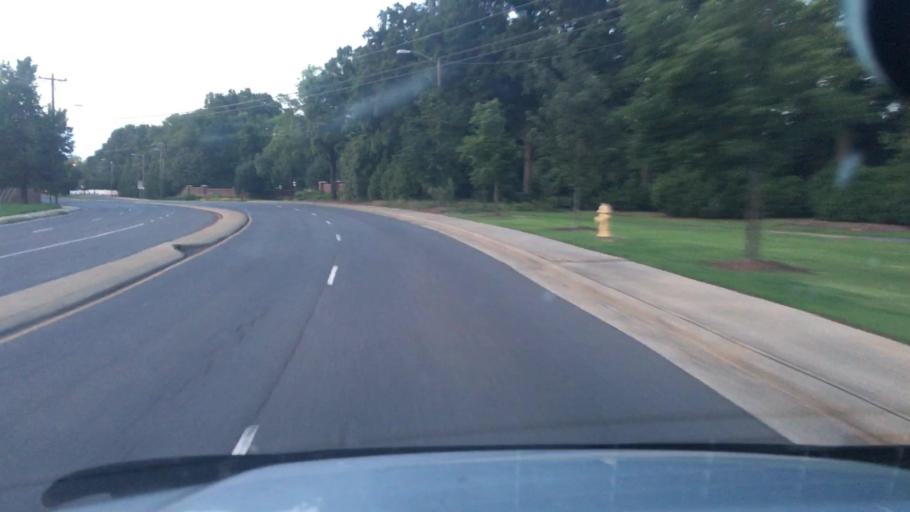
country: US
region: North Carolina
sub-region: Mecklenburg County
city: Pineville
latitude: 35.1062
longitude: -80.8270
